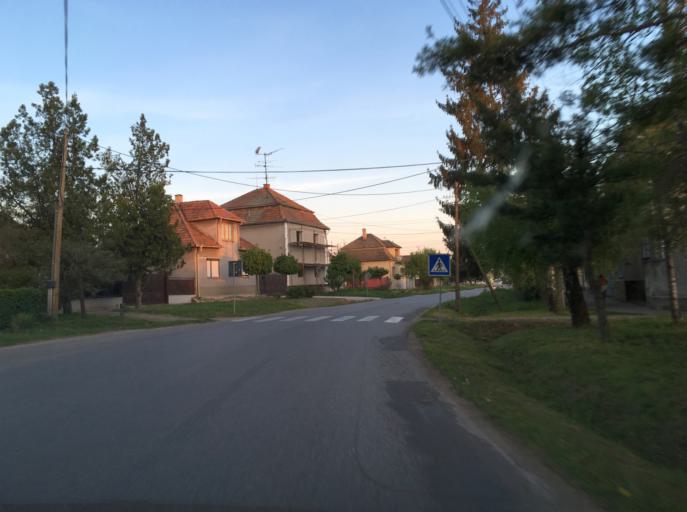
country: SK
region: Nitriansky
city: Kolarovo
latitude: 47.9140
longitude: 18.0001
